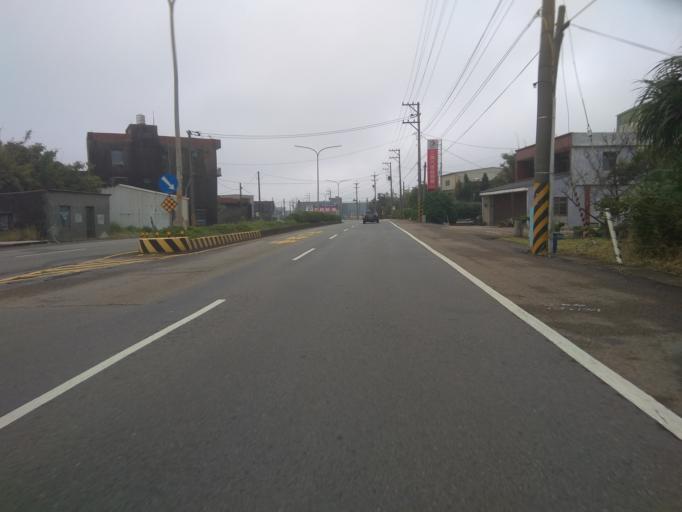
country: TW
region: Taiwan
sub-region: Hsinchu
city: Zhubei
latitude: 25.0056
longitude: 121.0416
